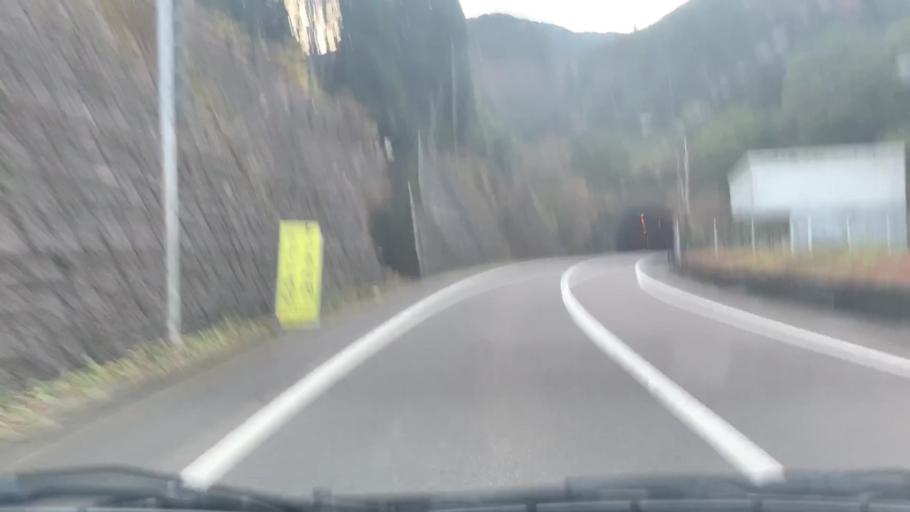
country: JP
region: Saga Prefecture
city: Kashima
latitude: 32.9986
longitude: 130.0624
